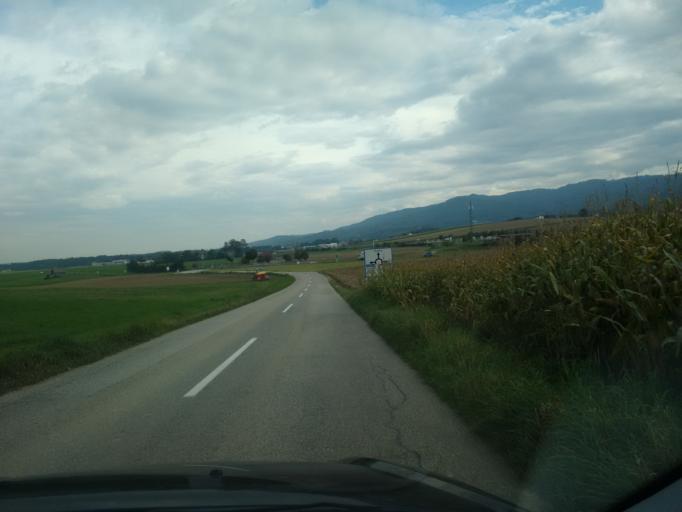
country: AT
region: Upper Austria
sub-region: Politischer Bezirk Vocklabruck
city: Lenzing
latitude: 47.9590
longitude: 13.6380
